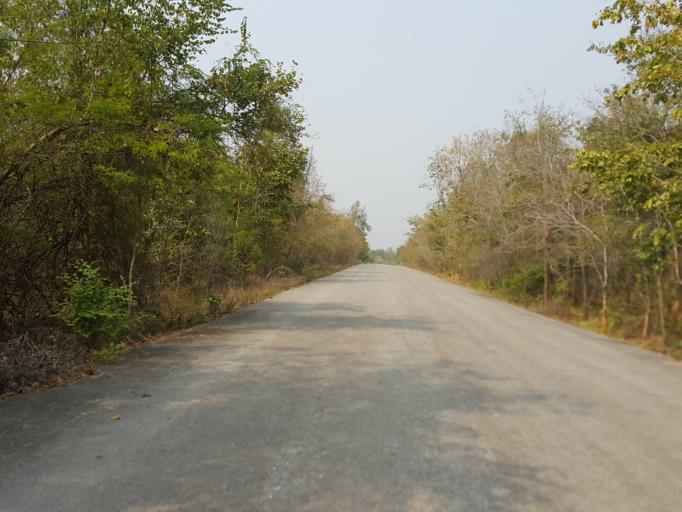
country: TH
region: Lampang
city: Mae Phrik
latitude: 17.4993
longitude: 99.0835
